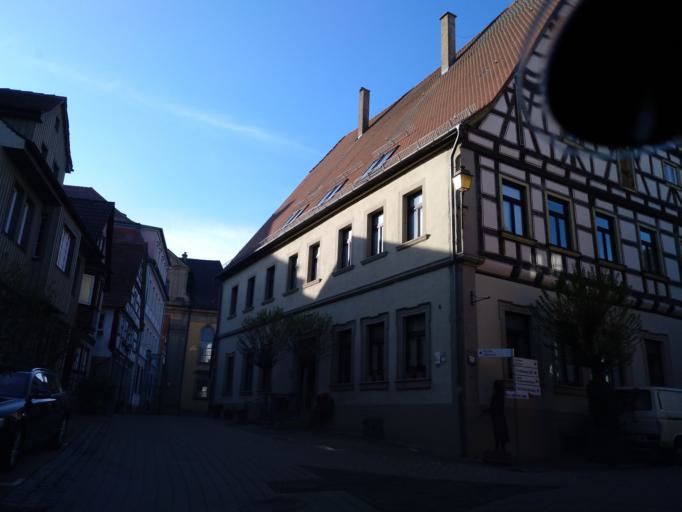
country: DE
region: Baden-Wuerttemberg
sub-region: Regierungsbezirk Stuttgart
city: Kirchberg an der Jagst
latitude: 49.2046
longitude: 9.9821
